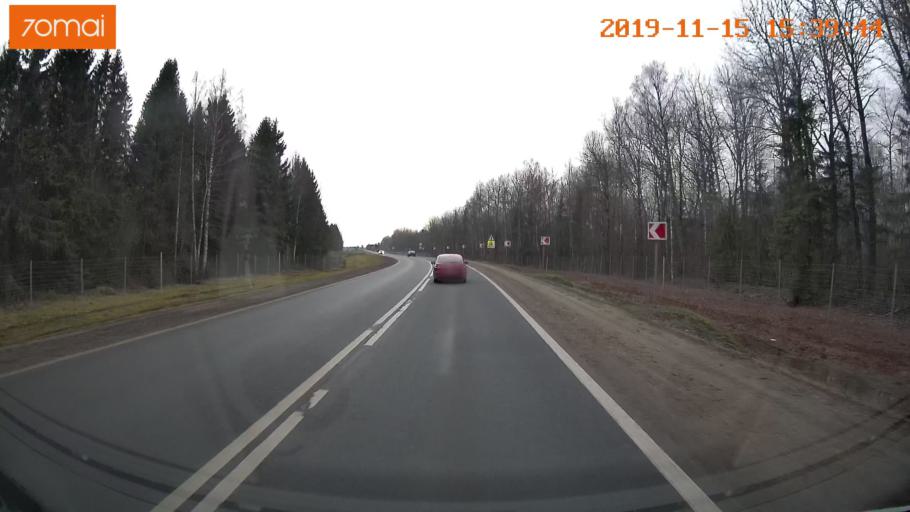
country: RU
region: Jaroslavl
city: Danilov
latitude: 58.0186
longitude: 40.0644
